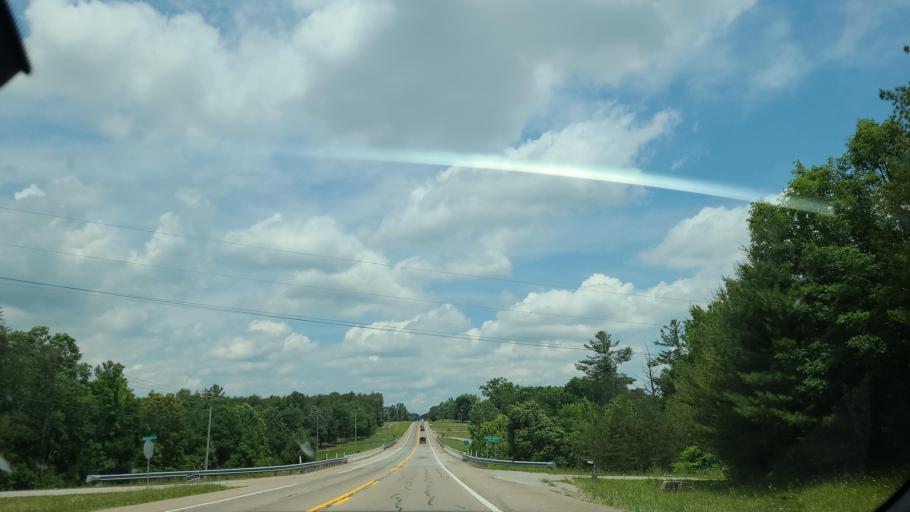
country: US
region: Tennessee
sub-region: Cumberland County
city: Lake Tansi
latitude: 35.8503
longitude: -85.0133
